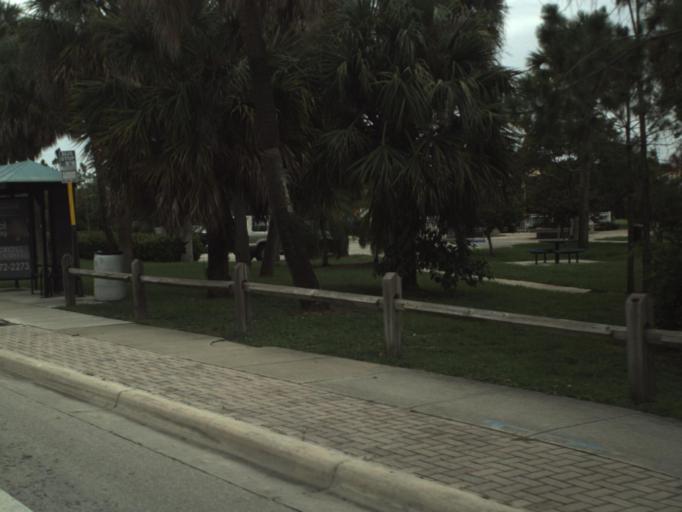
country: US
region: Florida
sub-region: Palm Beach County
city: Boynton Beach
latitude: 26.5042
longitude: -80.0598
